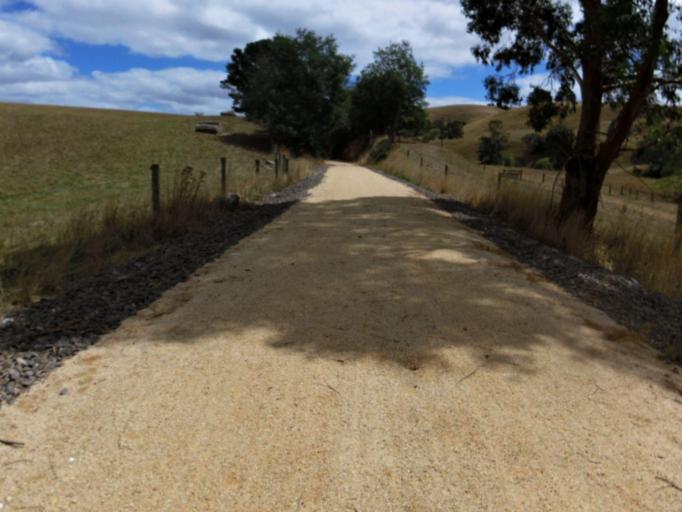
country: AU
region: Victoria
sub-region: Bass Coast
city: North Wonthaggi
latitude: -38.3932
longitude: 145.7287
